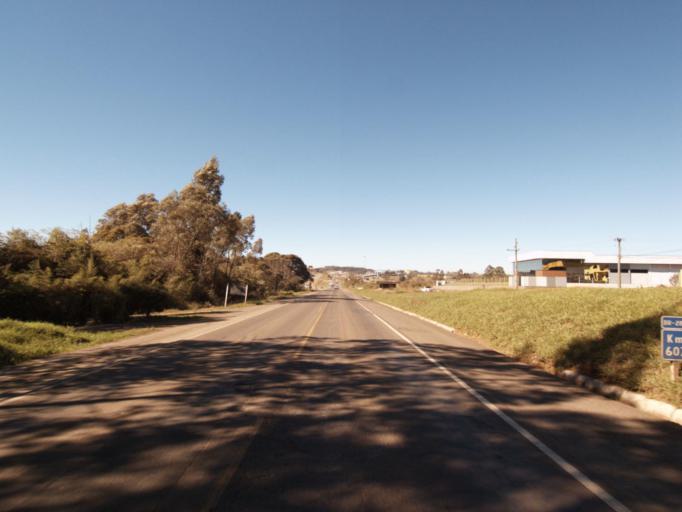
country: BR
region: Santa Catarina
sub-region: Sao Lourenco Do Oeste
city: Sao Lourenco dOeste
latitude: -26.7693
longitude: -53.2105
